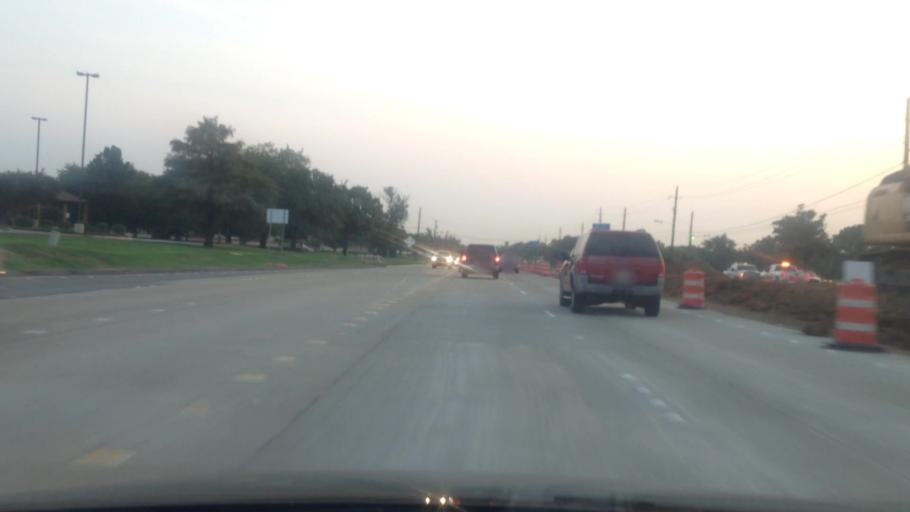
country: US
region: Texas
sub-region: Tarrant County
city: Colleyville
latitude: 32.8932
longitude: -97.1474
